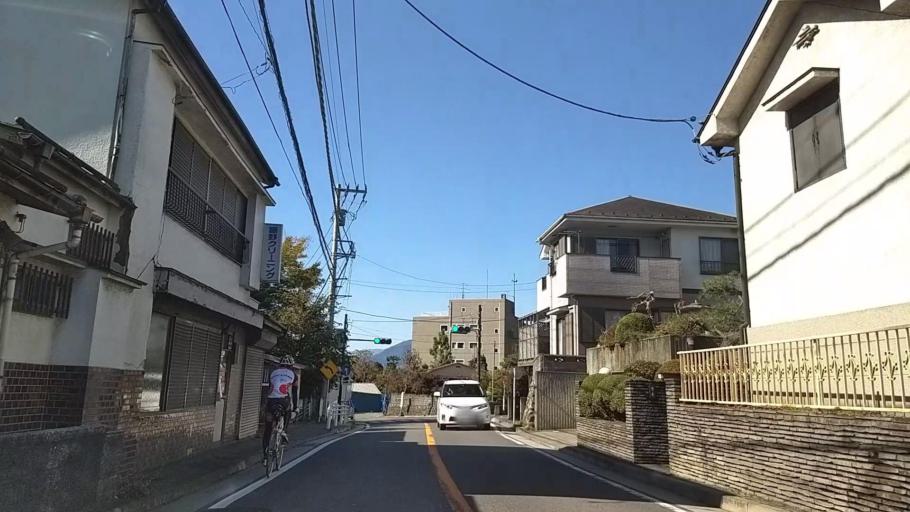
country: JP
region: Yamanashi
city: Uenohara
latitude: 35.6147
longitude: 139.1568
